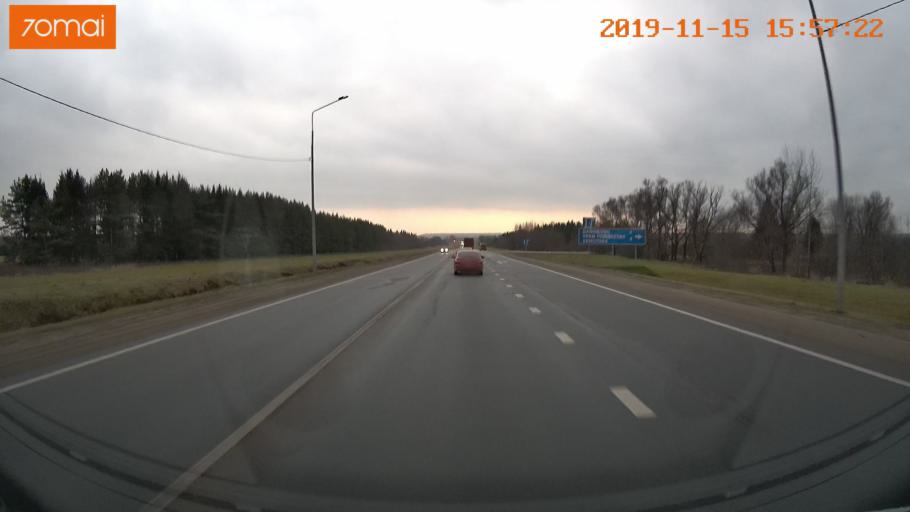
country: RU
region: Jaroslavl
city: Yaroslavl
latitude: 57.8311
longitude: 39.9643
